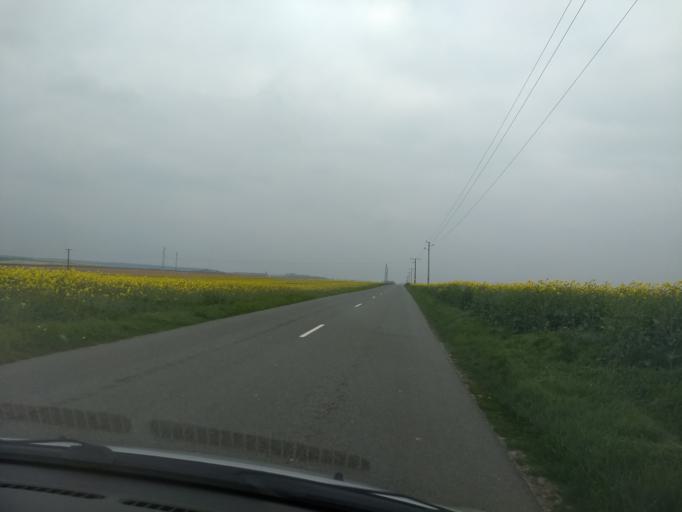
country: FR
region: Nord-Pas-de-Calais
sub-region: Departement du Pas-de-Calais
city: Mont-Saint-Eloi
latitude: 50.3512
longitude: 2.7199
